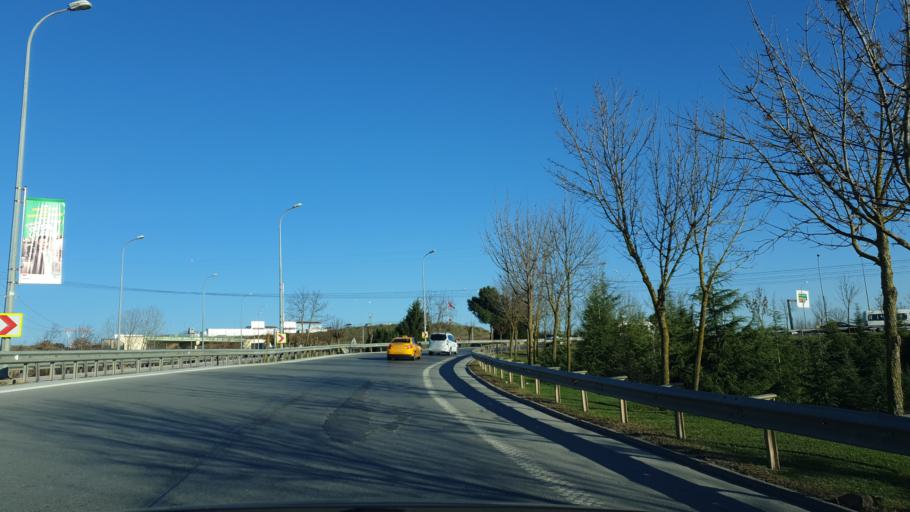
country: TR
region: Istanbul
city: Pendik
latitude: 40.9161
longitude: 29.3253
